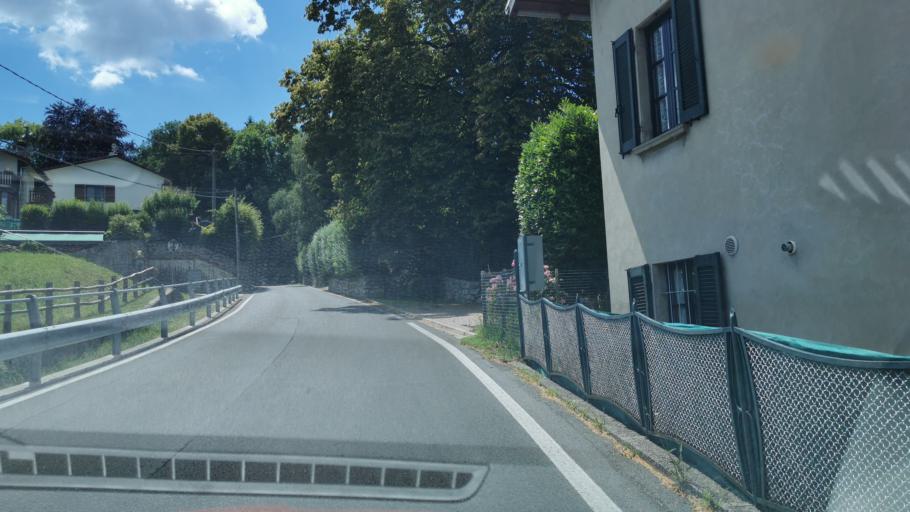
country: IT
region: Lombardy
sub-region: Provincia di Como
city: Pellio Intelvi
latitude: 45.9767
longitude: 9.0522
